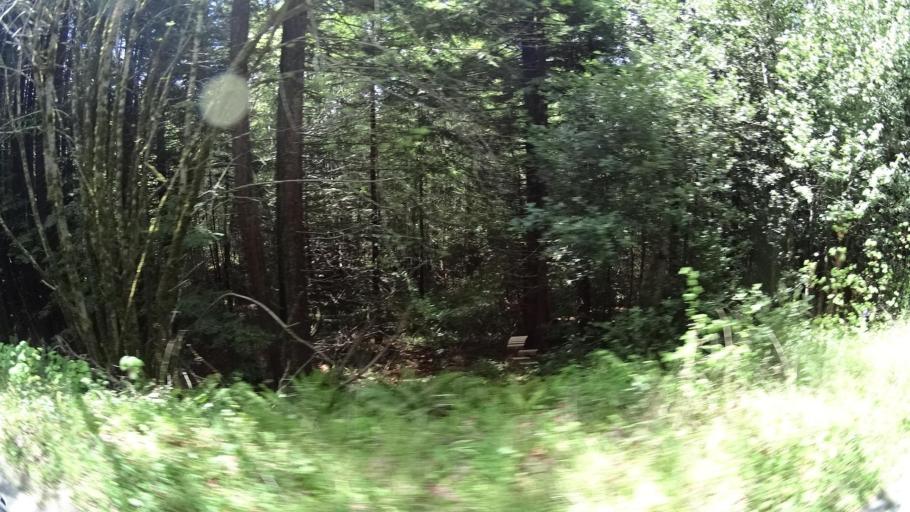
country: US
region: California
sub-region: Humboldt County
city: Blue Lake
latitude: 40.8258
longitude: -123.8937
